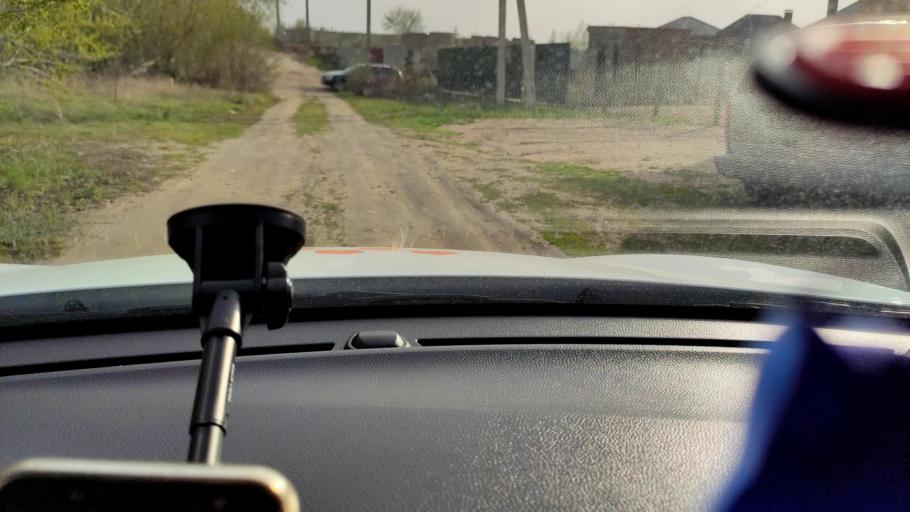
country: RU
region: Voronezj
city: Pridonskoy
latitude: 51.6977
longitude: 39.0700
